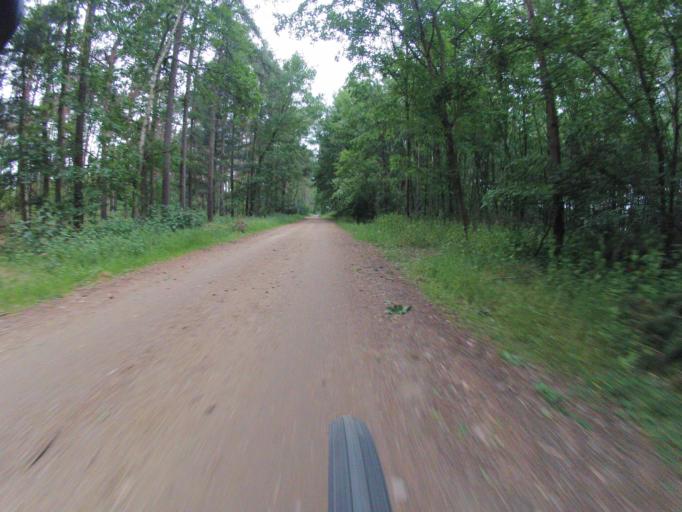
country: DE
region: North Rhine-Westphalia
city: Emsdetten
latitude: 52.2206
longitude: 7.5478
